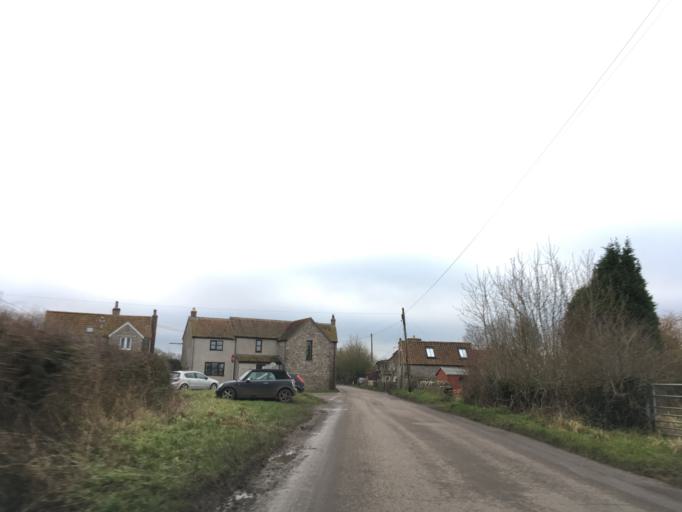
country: GB
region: England
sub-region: South Gloucestershire
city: Tytherington
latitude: 51.5750
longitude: -2.4961
